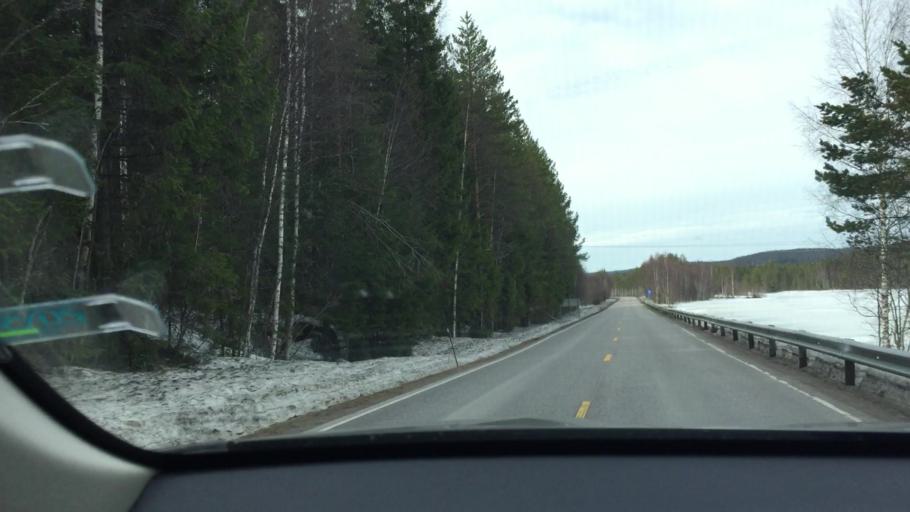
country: NO
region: Hedmark
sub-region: Trysil
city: Innbygda
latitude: 61.0684
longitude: 12.5793
